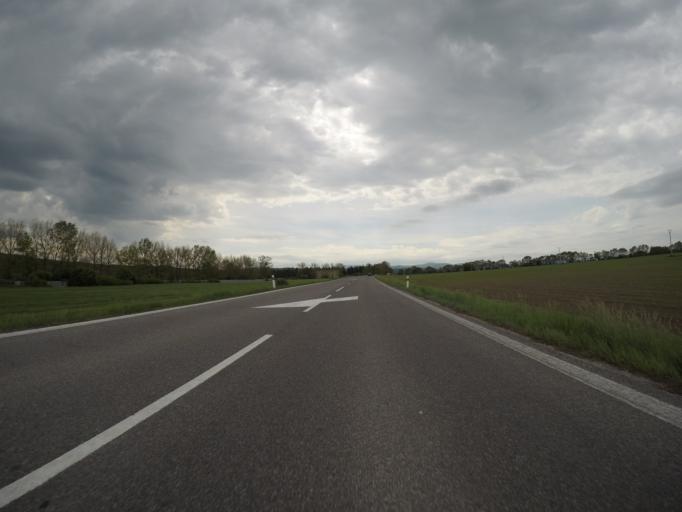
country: SK
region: Banskobystricky
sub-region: Okres Banska Bystrica
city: Banska Bystrica
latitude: 48.6642
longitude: 19.1410
